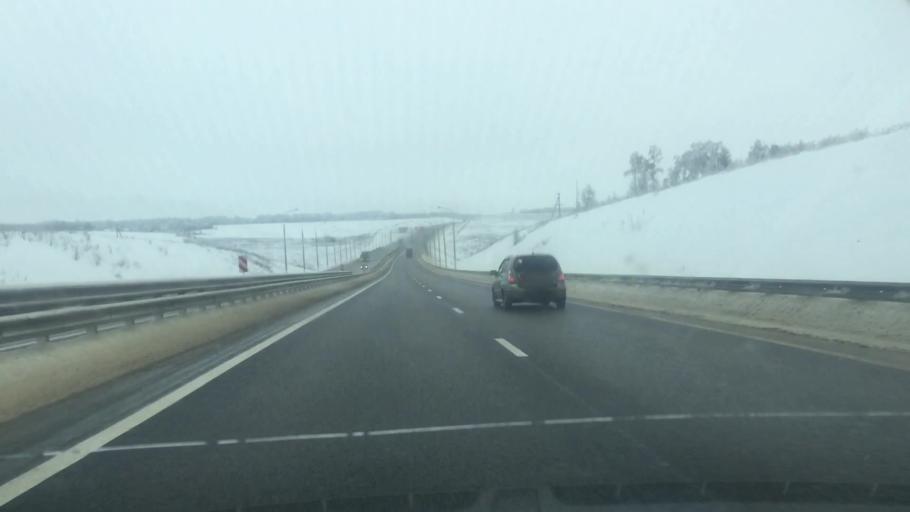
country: RU
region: Lipetsk
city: Stanovoye
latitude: 52.8687
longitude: 38.2827
